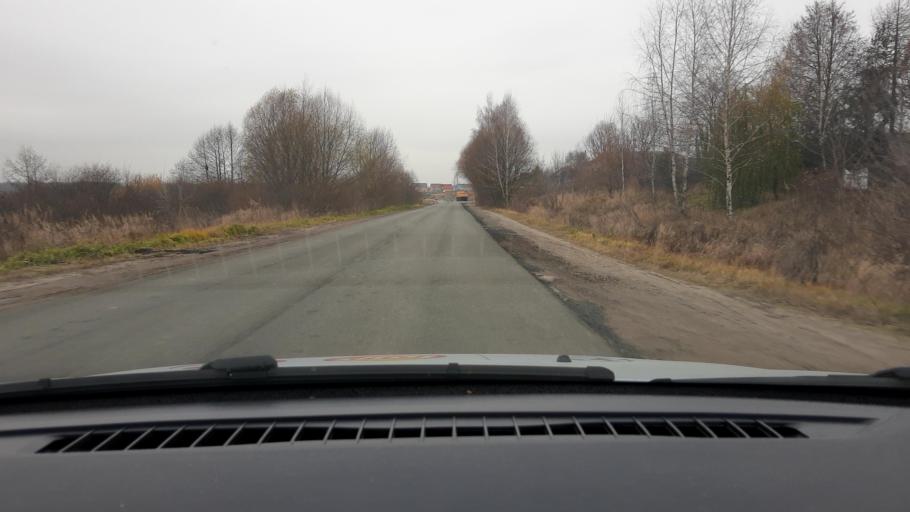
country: RU
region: Nizjnij Novgorod
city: Neklyudovo
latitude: 56.4207
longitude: 43.9600
